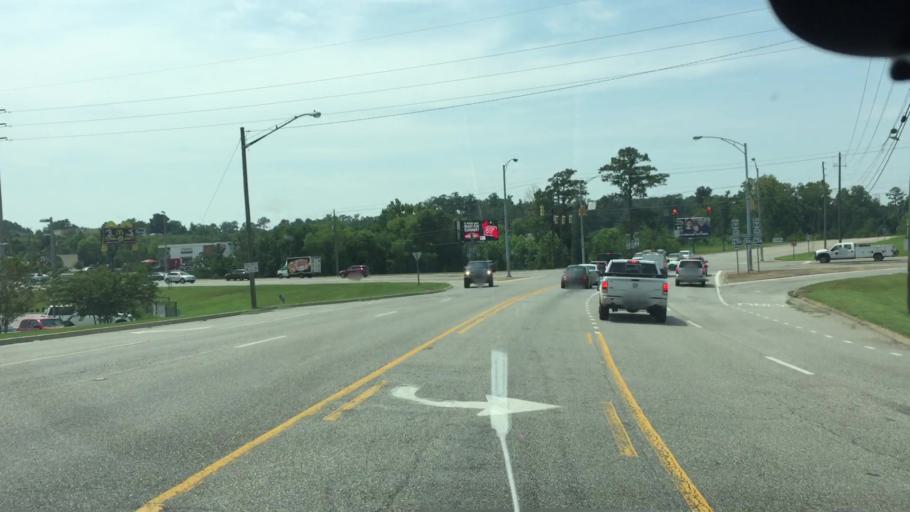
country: US
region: Alabama
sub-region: Coffee County
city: Enterprise
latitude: 31.3297
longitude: -85.8381
